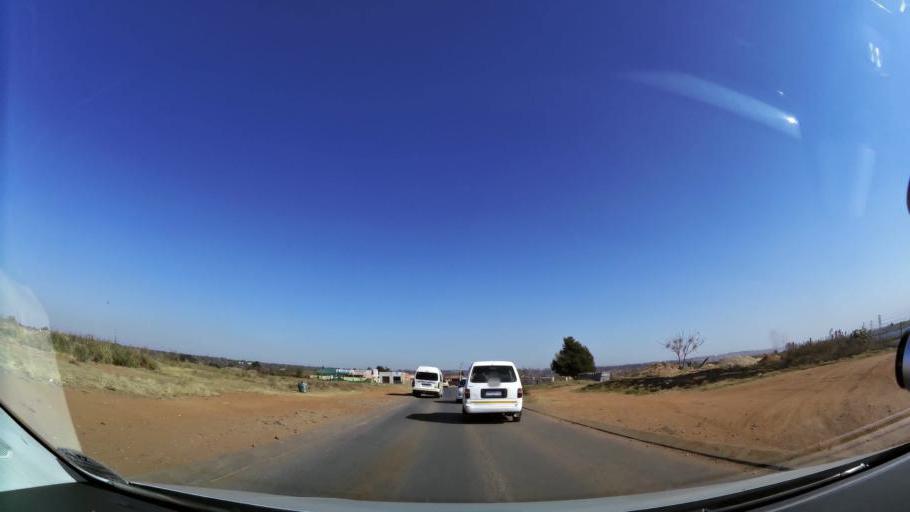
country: ZA
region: Gauteng
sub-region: Ekurhuleni Metropolitan Municipality
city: Tembisa
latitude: -26.0292
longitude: 28.2336
